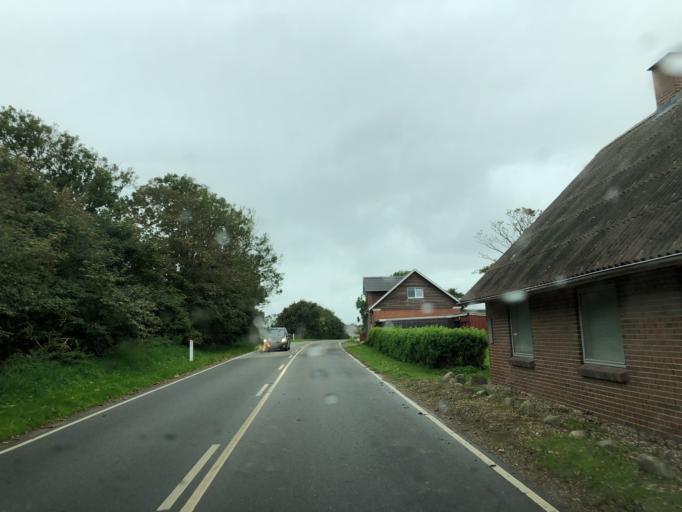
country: DK
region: North Denmark
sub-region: Thisted Kommune
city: Hurup
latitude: 56.7198
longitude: 8.3803
